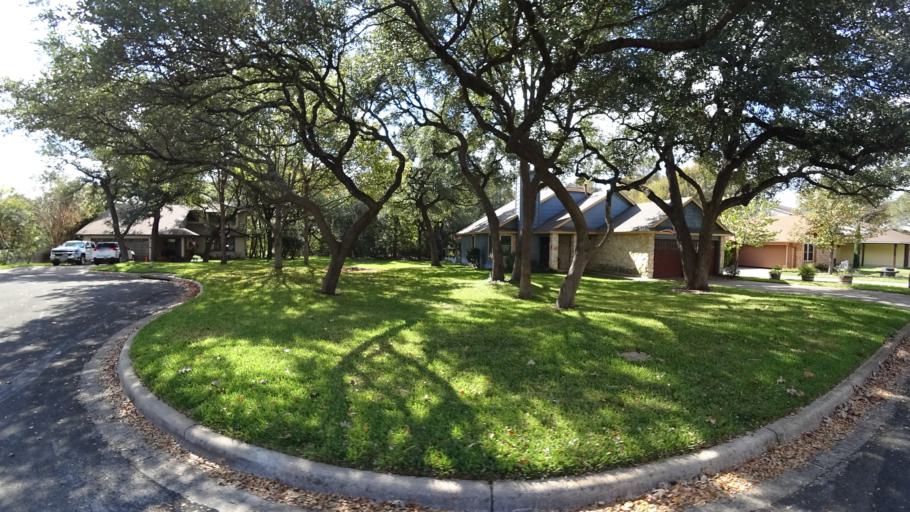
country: US
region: Texas
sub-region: Travis County
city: Wells Branch
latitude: 30.4252
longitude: -97.7198
